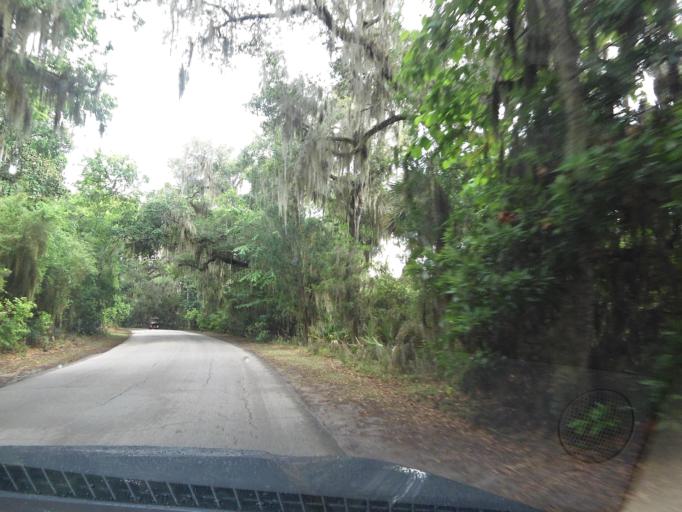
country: US
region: Florida
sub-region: Nassau County
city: Fernandina Beach
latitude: 30.6891
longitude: -81.4387
